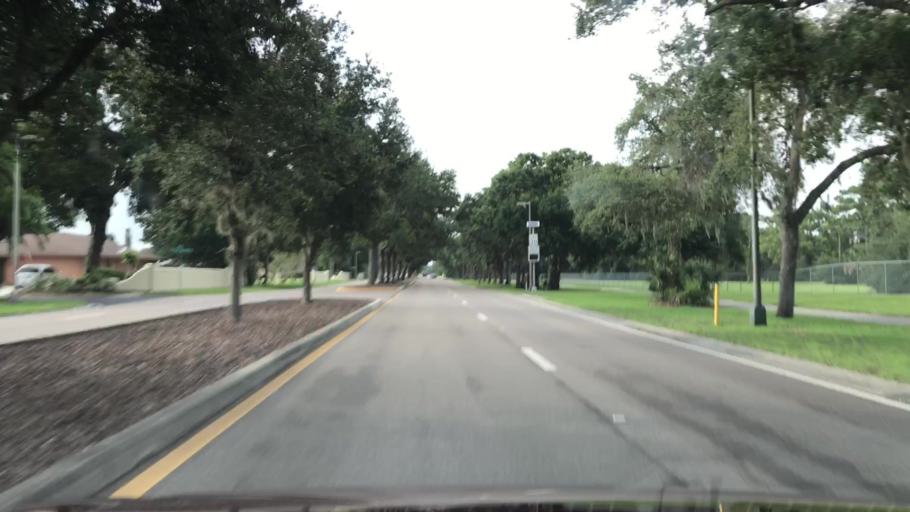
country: US
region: Florida
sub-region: Sarasota County
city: Plantation
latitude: 27.0730
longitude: -82.3889
